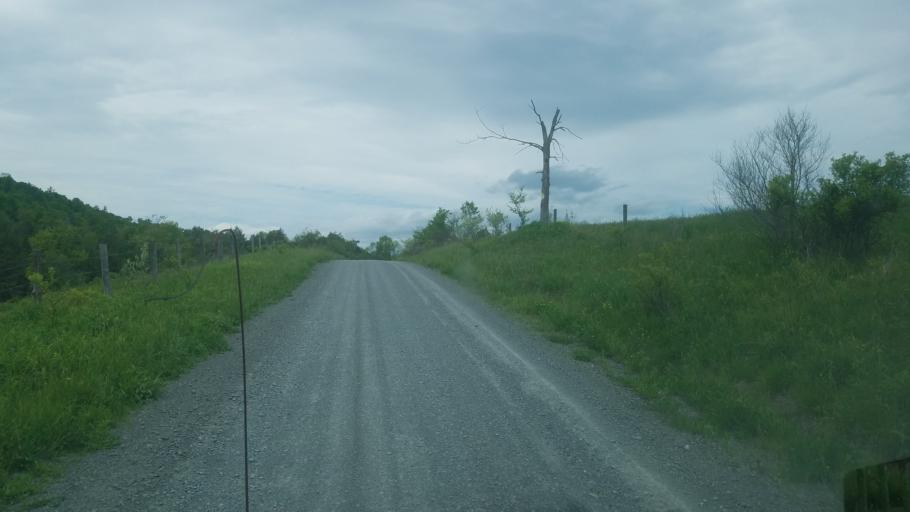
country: US
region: Pennsylvania
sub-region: Tioga County
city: Westfield
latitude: 41.8455
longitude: -77.6027
